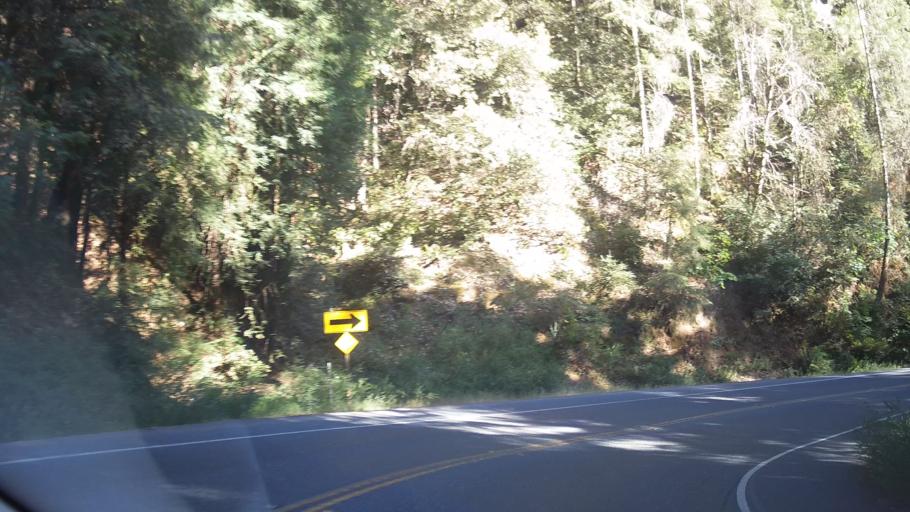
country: US
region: California
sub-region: Mendocino County
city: Brooktrails
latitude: 39.3687
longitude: -123.4964
